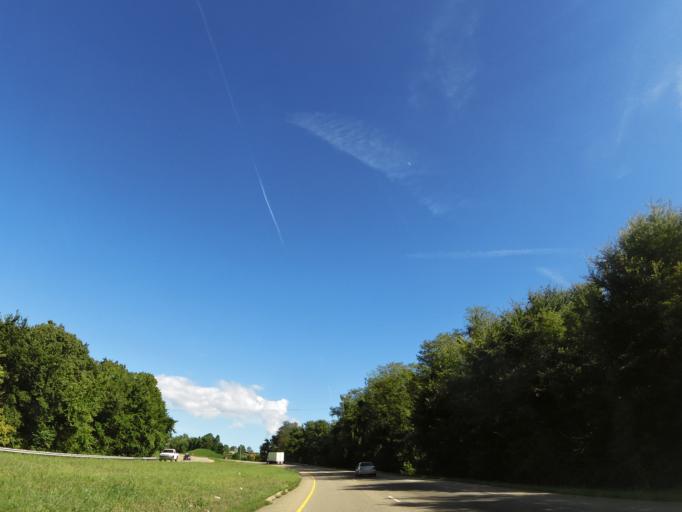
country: US
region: Tennessee
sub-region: Greene County
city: Mosheim
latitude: 36.1952
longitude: -82.9951
